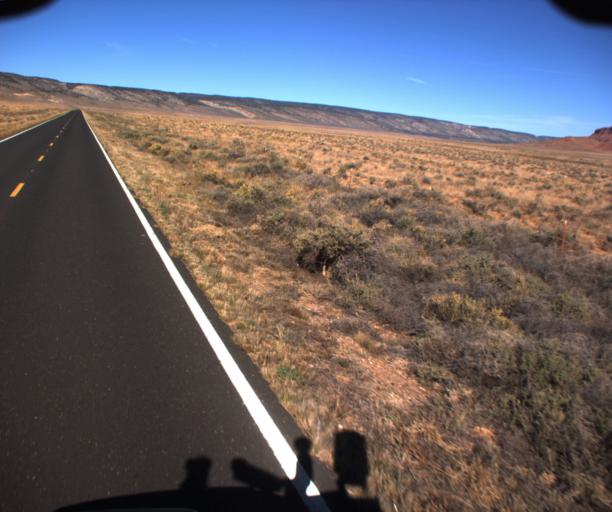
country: US
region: Arizona
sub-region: Coconino County
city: Fredonia
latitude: 36.7199
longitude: -112.0092
